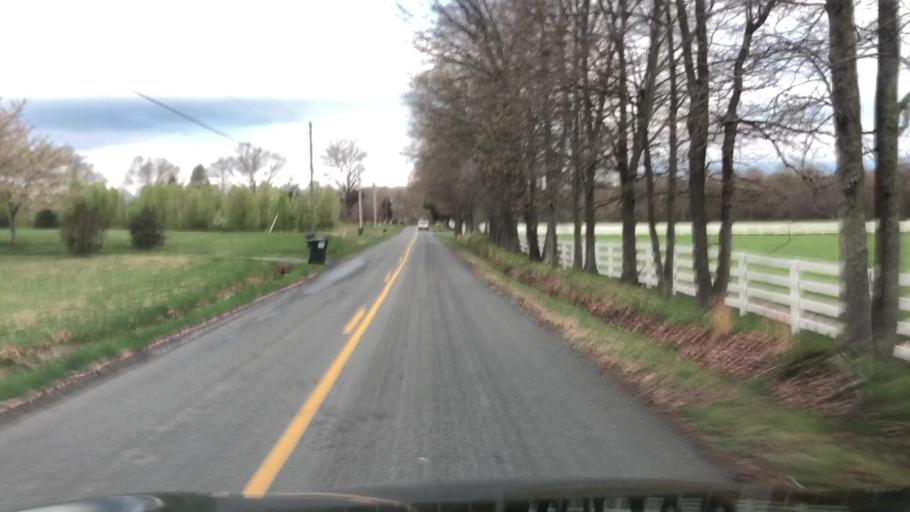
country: US
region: Virginia
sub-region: Fauquier County
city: New Baltimore
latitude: 38.7346
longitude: -77.6728
